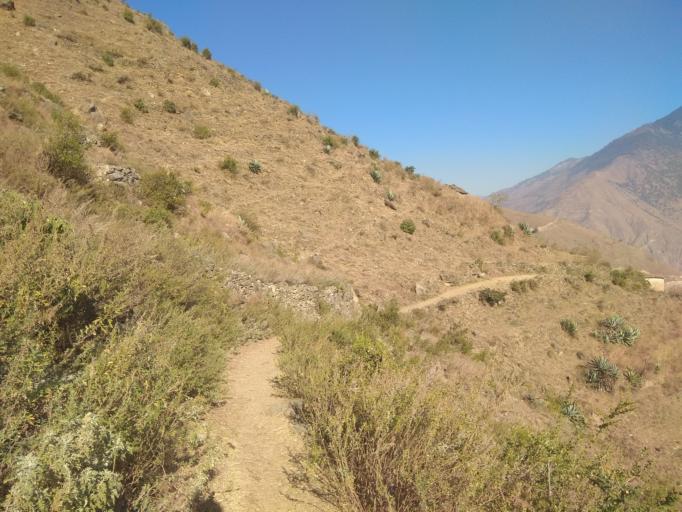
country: NP
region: Mid Western
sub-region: Karnali Zone
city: Jumla
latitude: 29.3153
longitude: 81.7412
